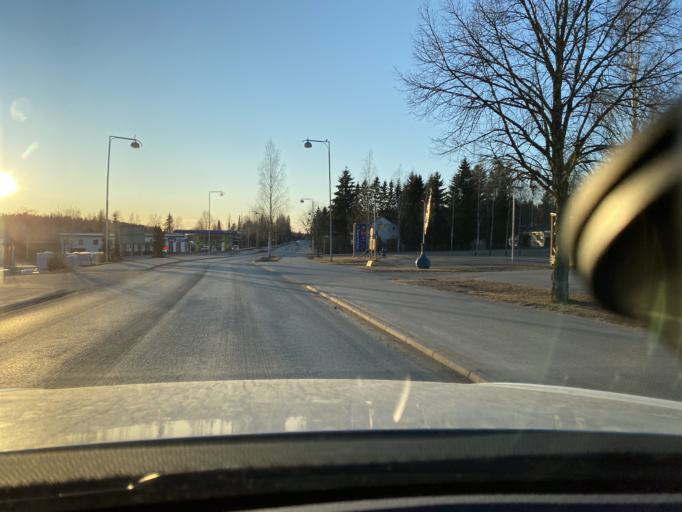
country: FI
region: Pirkanmaa
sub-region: Lounais-Pirkanmaa
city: Punkalaidun
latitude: 61.1122
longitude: 23.1048
